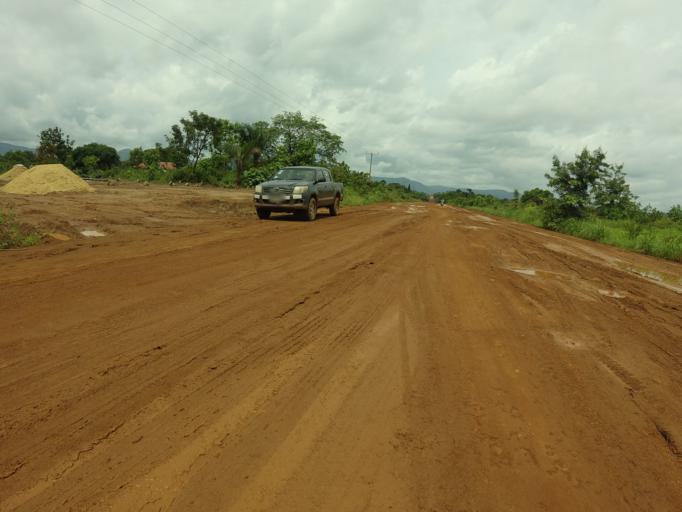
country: GH
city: Kpandae
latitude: 8.2820
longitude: 0.5035
